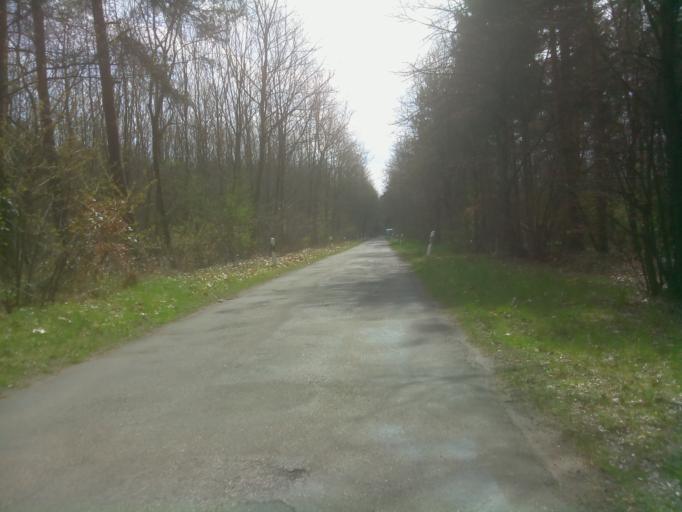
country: DE
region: Hesse
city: Lampertheim
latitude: 49.5631
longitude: 8.4925
